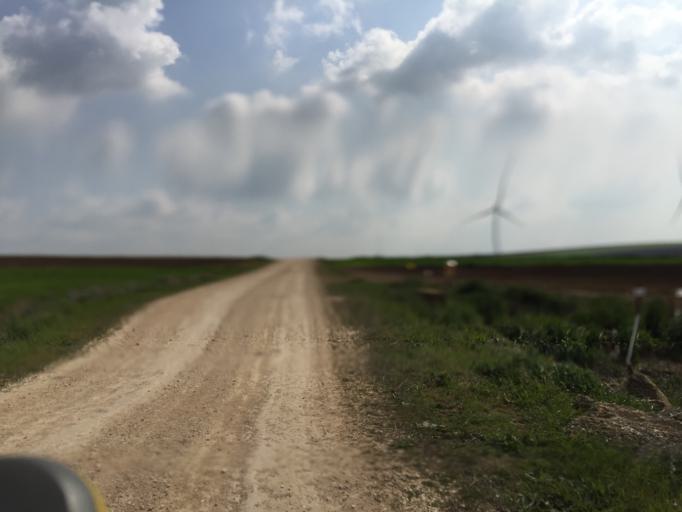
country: ES
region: Andalusia
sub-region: Provincia de Cadiz
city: Benalup-Casas Viejas
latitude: 36.3286
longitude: -5.9041
